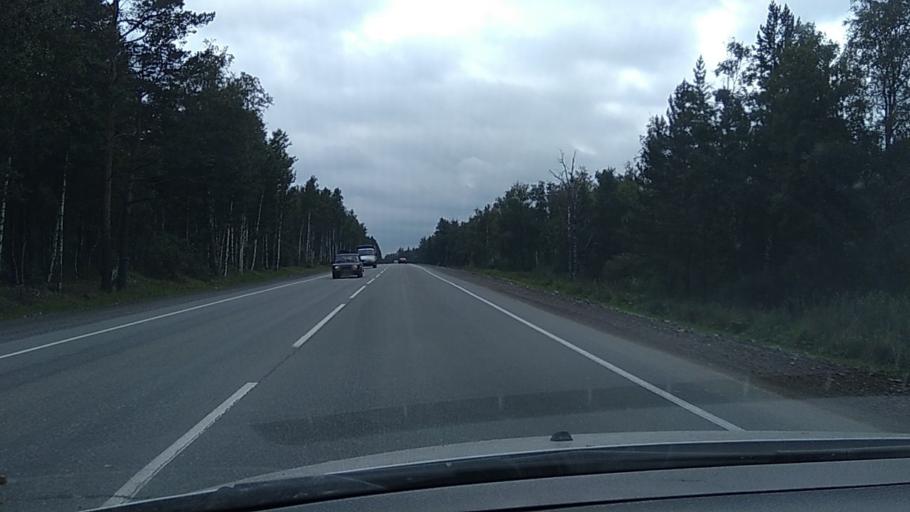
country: RU
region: Chelyabinsk
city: Zlatoust
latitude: 55.0375
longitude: 59.7240
